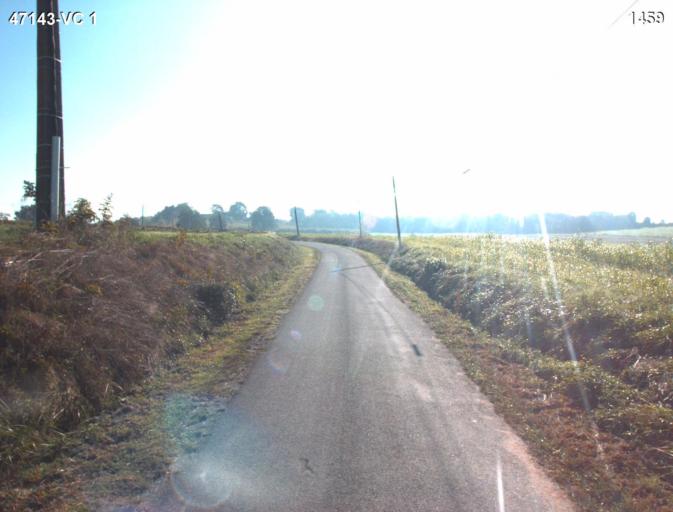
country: FR
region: Aquitaine
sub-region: Departement du Lot-et-Garonne
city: Vianne
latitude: 44.1909
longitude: 0.3241
